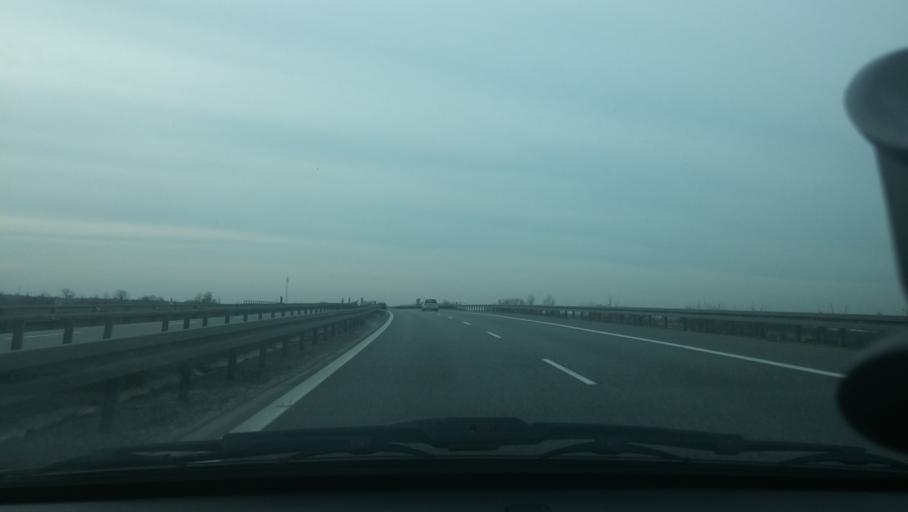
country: PL
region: Masovian Voivodeship
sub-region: Powiat wolominski
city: Radzymin
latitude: 52.4342
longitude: 21.2304
